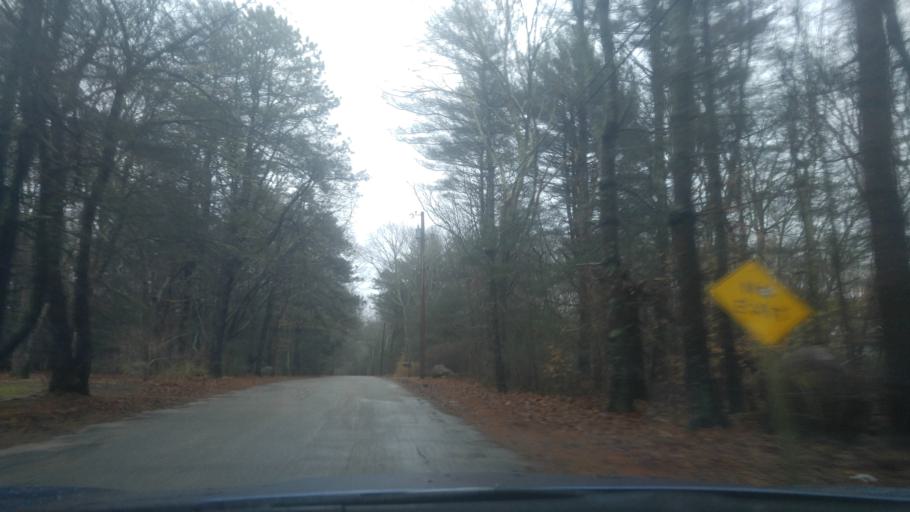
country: US
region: Rhode Island
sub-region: Washington County
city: Charlestown
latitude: 41.4386
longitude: -71.6092
